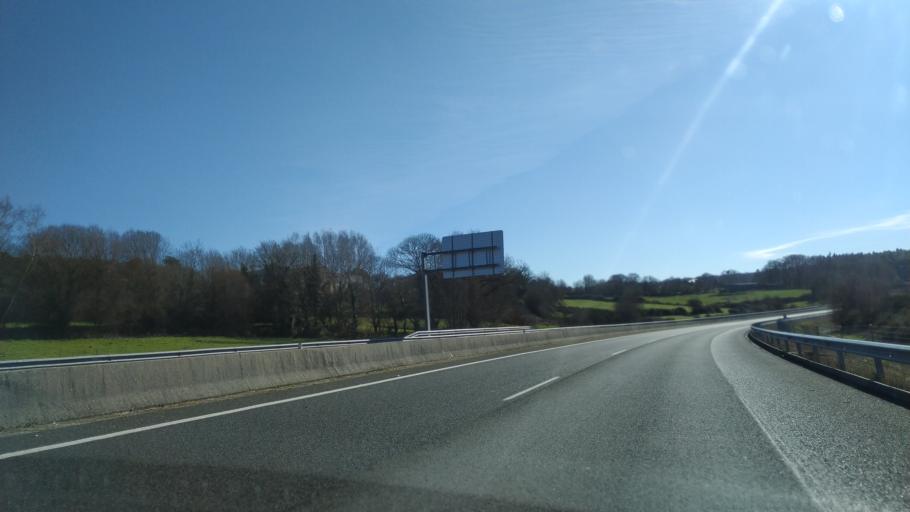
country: ES
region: Galicia
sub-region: Provincia de Pontevedra
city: Lalin
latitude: 42.6695
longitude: -8.1503
